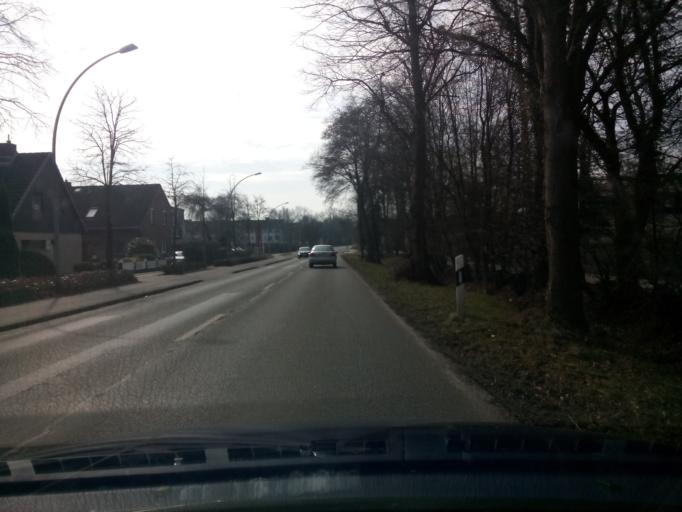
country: DE
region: Lower Saxony
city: Osterholz-Scharmbeck
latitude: 53.2199
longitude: 8.7820
